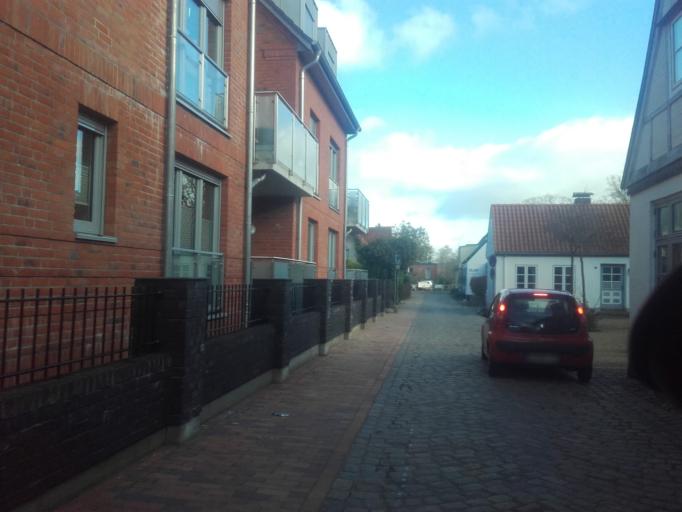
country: DE
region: Schleswig-Holstein
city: Busdorf
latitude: 54.5059
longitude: 9.5414
